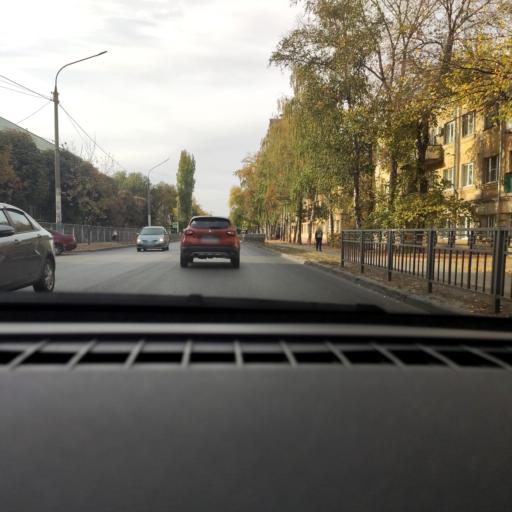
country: RU
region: Voronezj
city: Somovo
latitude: 51.7207
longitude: 39.2706
